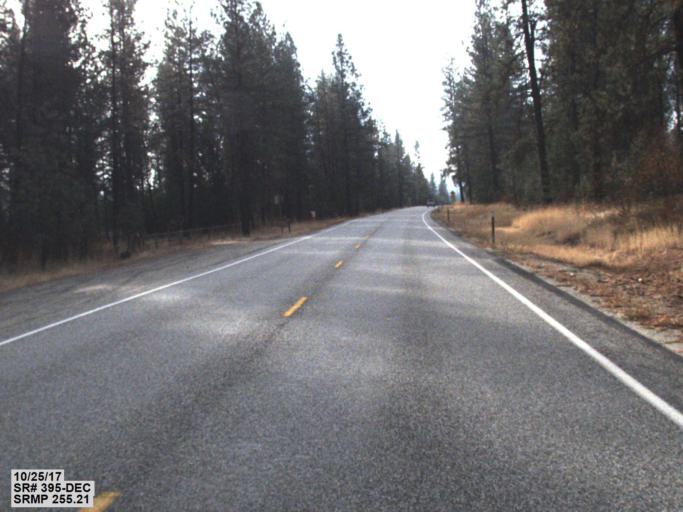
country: US
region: Washington
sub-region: Stevens County
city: Kettle Falls
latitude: 48.8046
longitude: -118.1624
